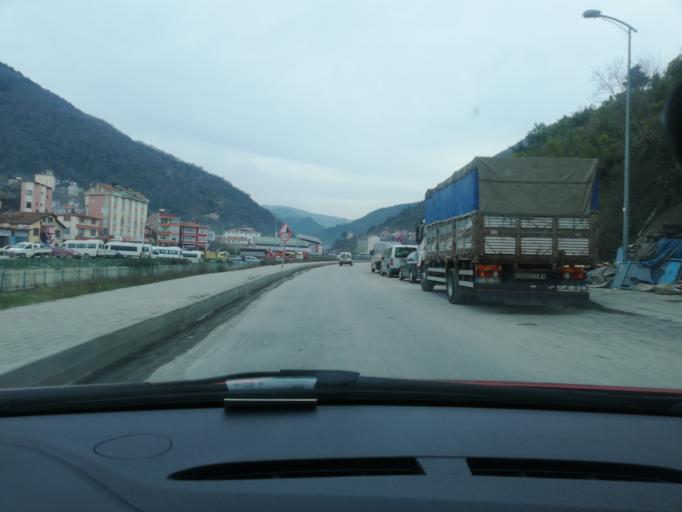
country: TR
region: Kastamonu
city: Inebolu
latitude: 41.9654
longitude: 33.7513
